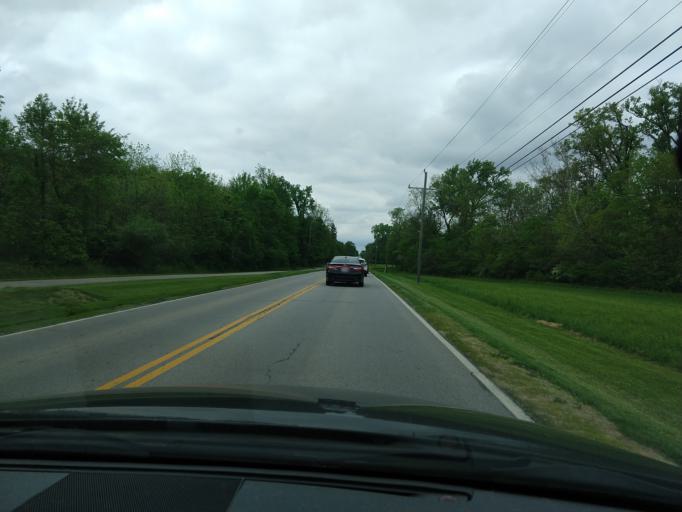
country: US
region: Indiana
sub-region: Hamilton County
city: Westfield
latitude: 40.0231
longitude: -86.1275
